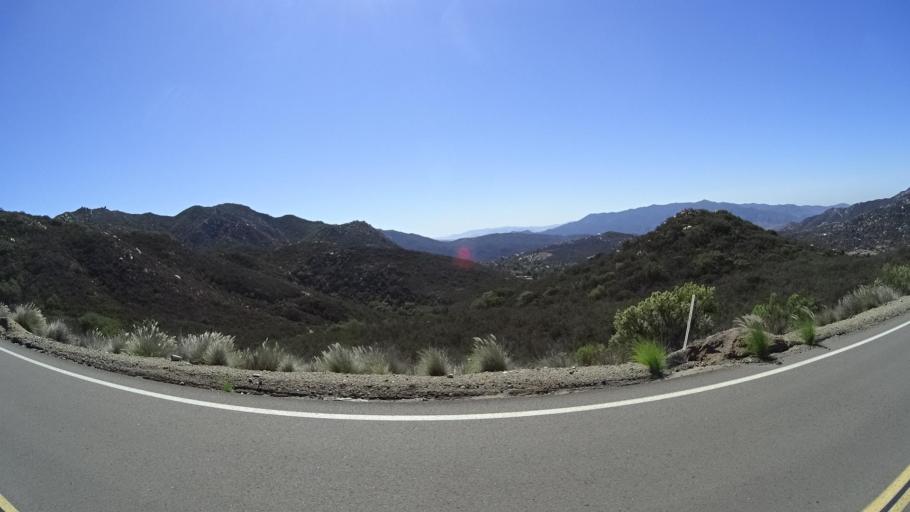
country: US
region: California
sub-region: San Diego County
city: Jamul
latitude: 32.7334
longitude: -116.8071
